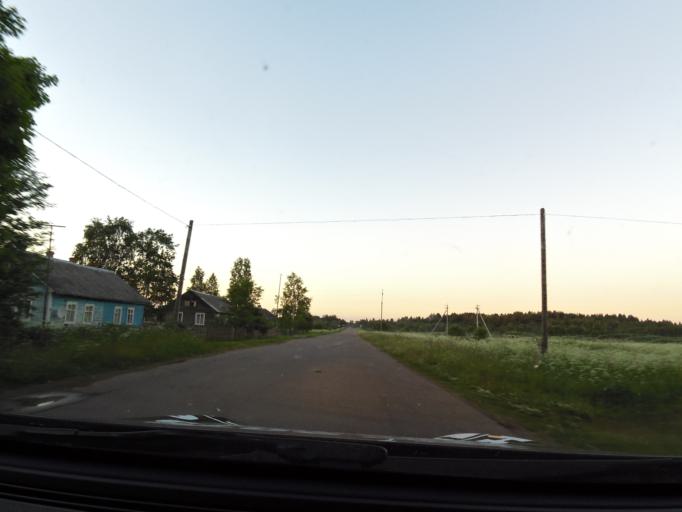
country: RU
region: Leningrad
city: Voznesen'ye
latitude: 60.8341
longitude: 35.7565
